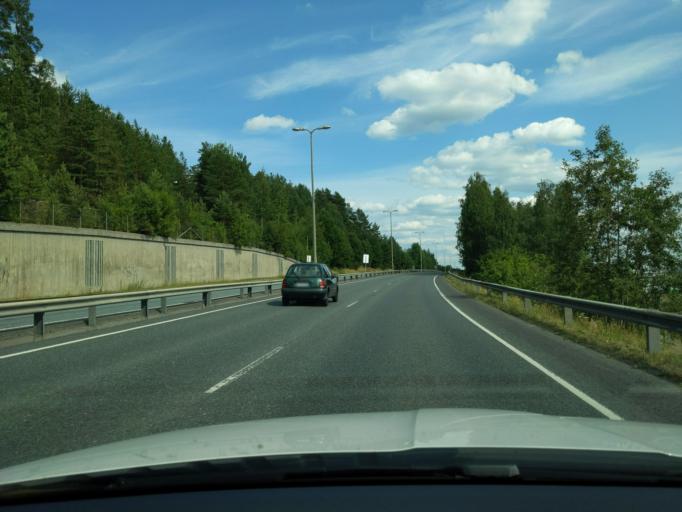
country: FI
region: Paijanne Tavastia
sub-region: Lahti
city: Lahti
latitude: 60.9765
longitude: 25.6822
